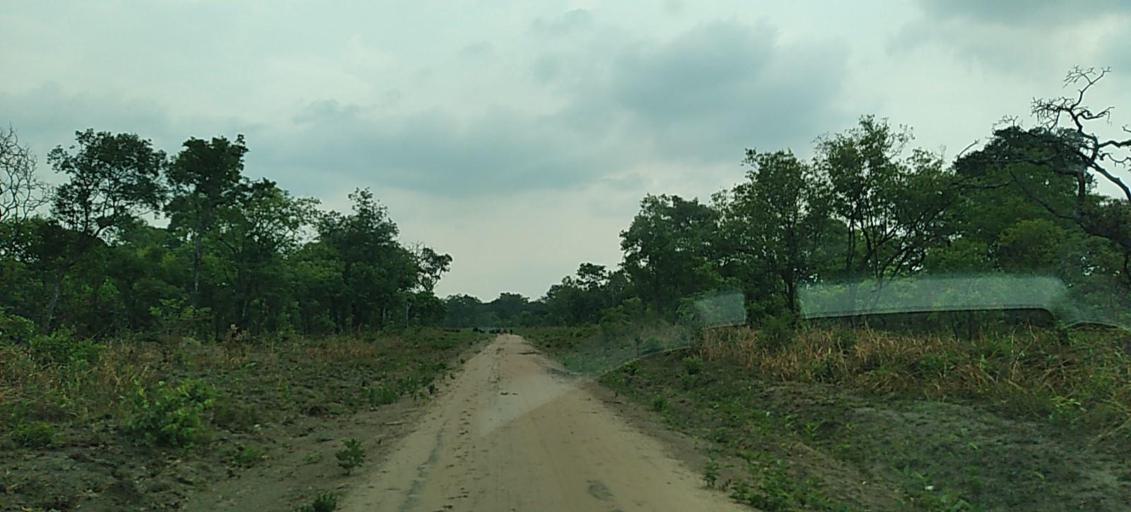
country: ZM
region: North-Western
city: Mwinilunga
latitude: -11.4072
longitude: 24.6237
